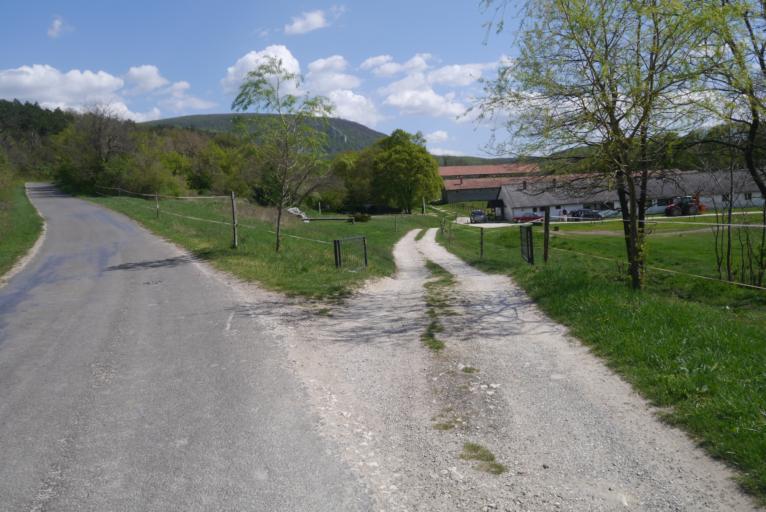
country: HU
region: Komarom-Esztergom
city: Kesztolc
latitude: 47.7122
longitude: 18.8149
